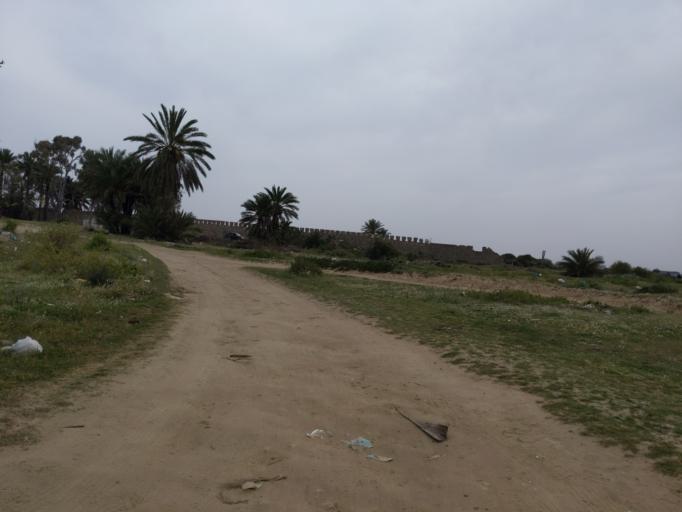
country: TN
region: Al Munastir
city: Saqanis
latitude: 35.7762
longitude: 10.7778
